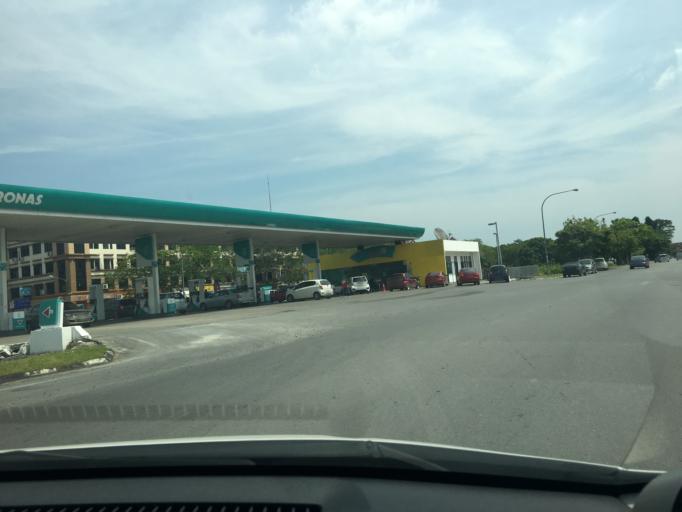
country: MY
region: Sarawak
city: Kuching
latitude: 1.5138
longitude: 110.3125
